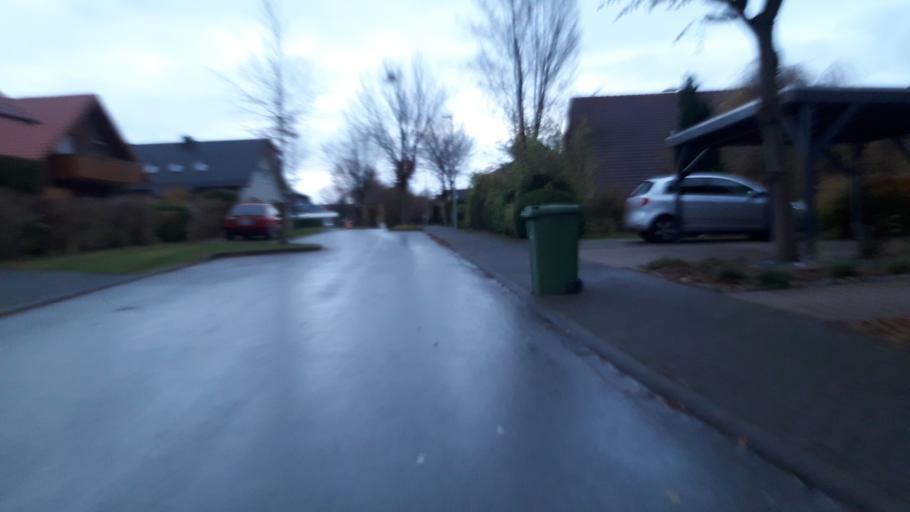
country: DE
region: North Rhine-Westphalia
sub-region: Regierungsbezirk Detmold
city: Altenbeken
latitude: 51.7543
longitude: 8.9493
